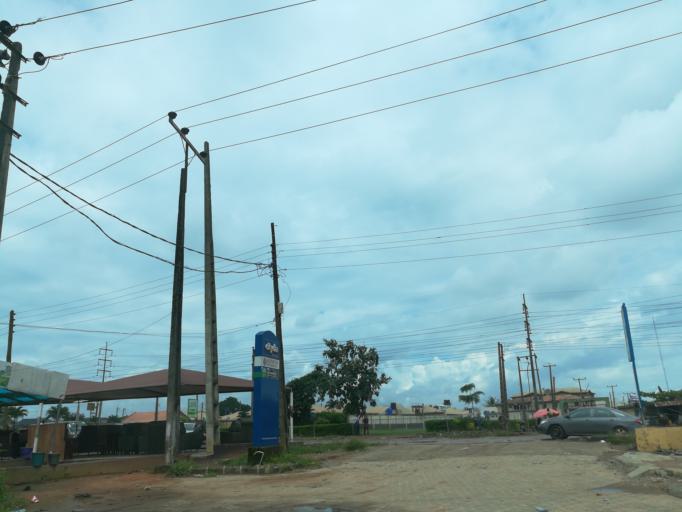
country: NG
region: Lagos
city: Ikorodu
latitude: 6.6382
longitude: 3.5135
